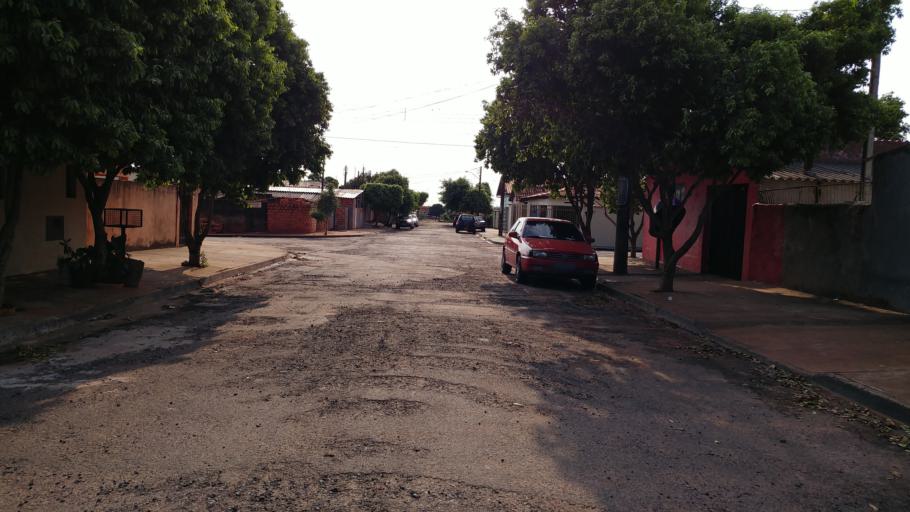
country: BR
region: Sao Paulo
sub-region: Paraguacu Paulista
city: Paraguacu Paulista
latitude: -22.4194
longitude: -50.5887
